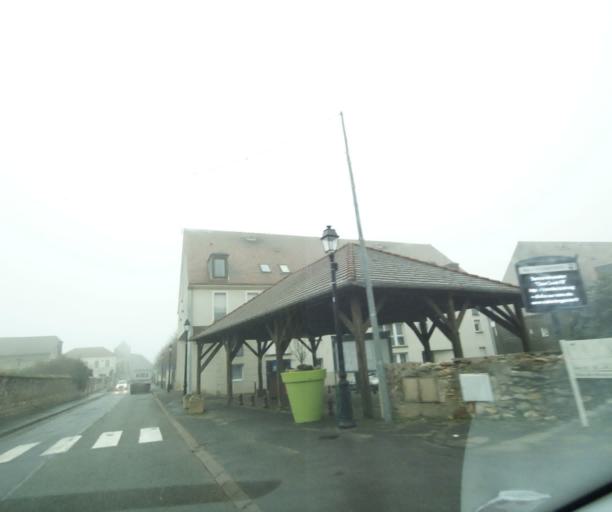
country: FR
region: Ile-de-France
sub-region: Departement de Seine-et-Marne
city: Longperrier
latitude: 49.0527
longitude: 2.6653
